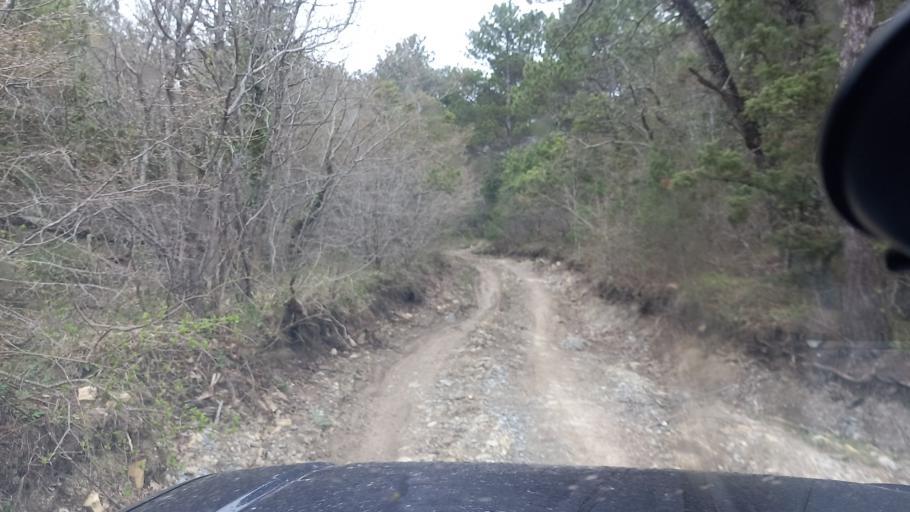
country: RU
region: Krasnodarskiy
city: Arkhipo-Osipovka
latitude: 44.3765
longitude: 38.4720
